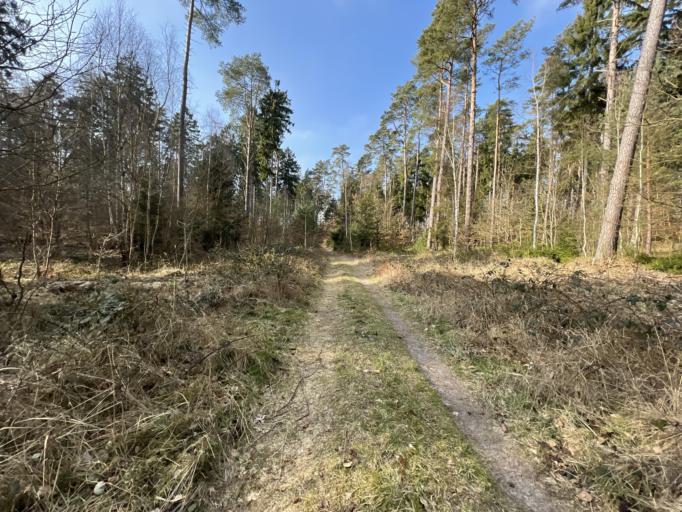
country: DE
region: Mecklenburg-Vorpommern
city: Sagard
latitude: 54.4788
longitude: 13.5587
